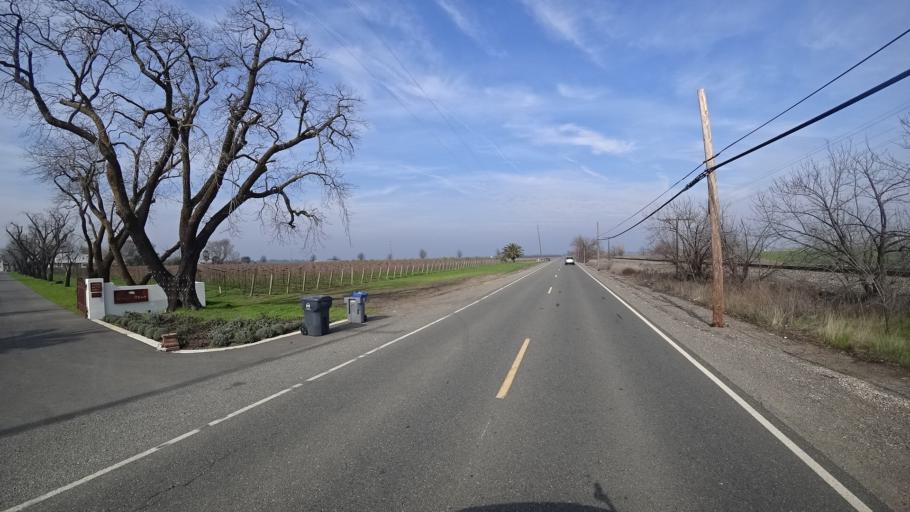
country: US
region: California
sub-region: Yolo County
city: Davis
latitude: 38.5794
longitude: -121.7491
